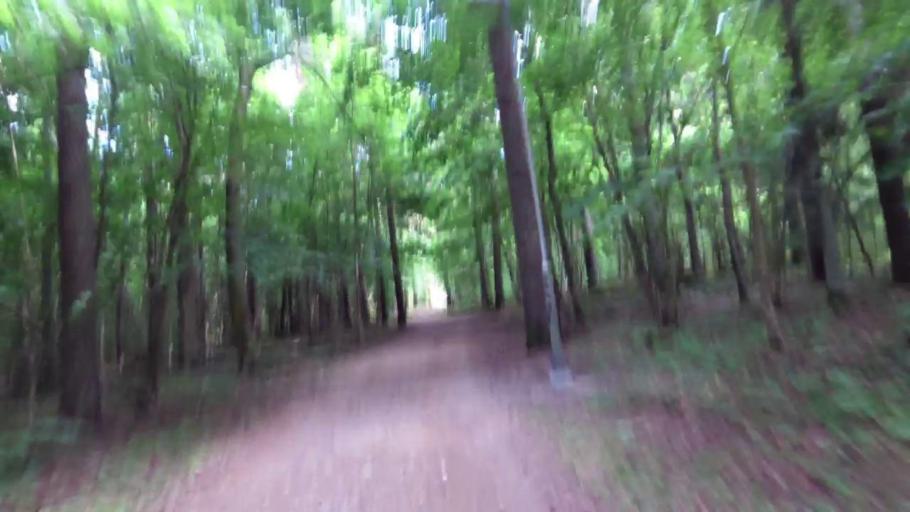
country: SE
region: OEstergoetland
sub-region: Linkopings Kommun
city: Linkoping
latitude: 58.4182
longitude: 15.5797
